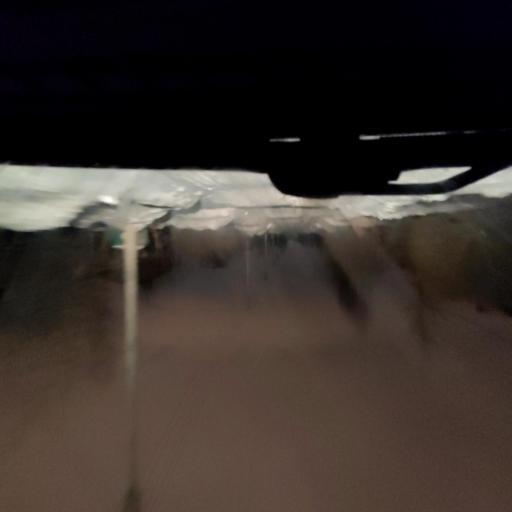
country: RU
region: Samara
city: Tol'yatti
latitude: 53.5706
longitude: 49.3300
